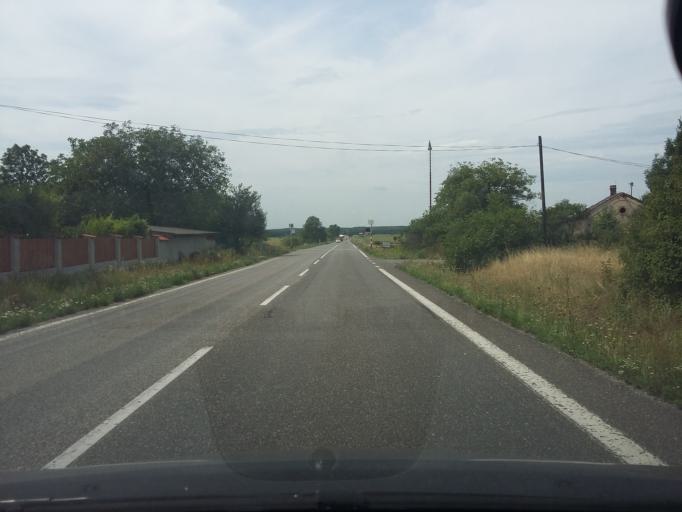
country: SK
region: Bratislavsky
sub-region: Okres Malacky
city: Malacky
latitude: 48.3788
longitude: 17.1223
